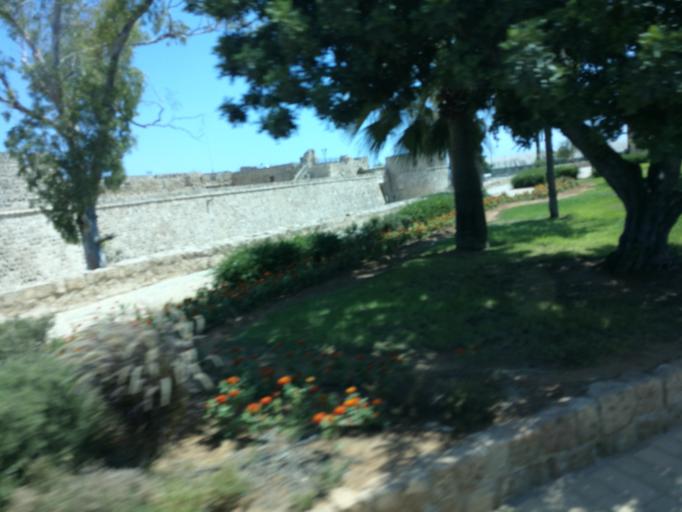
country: CY
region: Ammochostos
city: Famagusta
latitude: 35.1270
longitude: 33.9426
